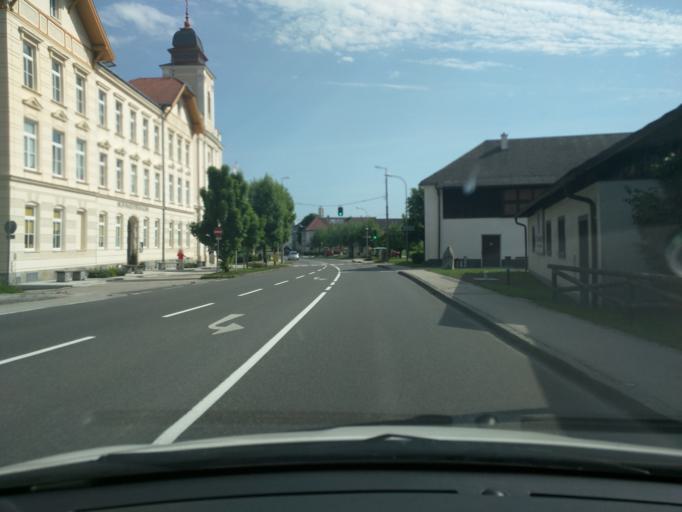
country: AT
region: Lower Austria
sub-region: Politischer Bezirk Amstetten
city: Kematen an der Ybbs
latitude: 48.0138
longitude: 14.7465
